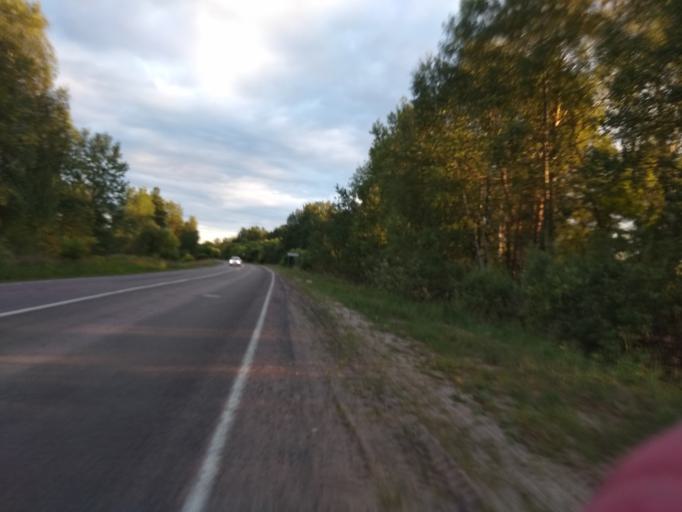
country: RU
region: Moskovskaya
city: Misheronskiy
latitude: 55.6055
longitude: 39.7097
